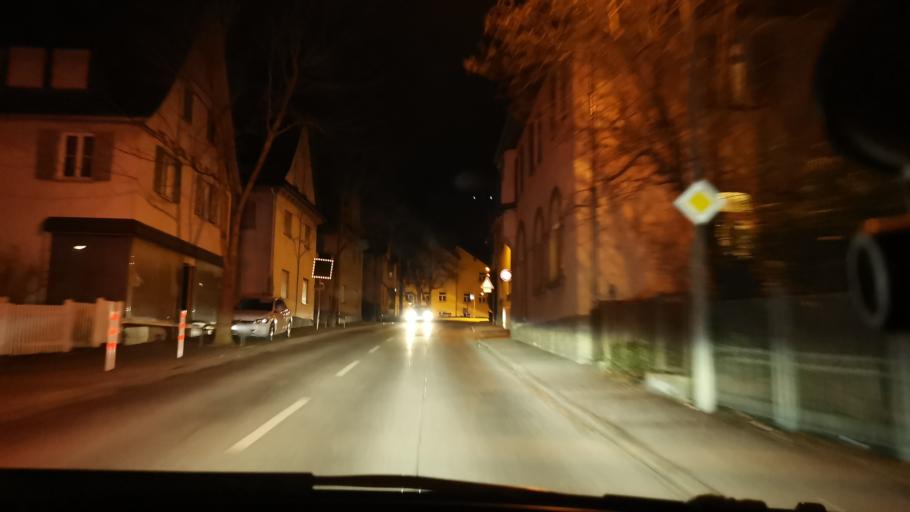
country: DE
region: Baden-Wuerttemberg
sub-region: Regierungsbezirk Stuttgart
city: Ehningen
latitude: 48.6968
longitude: 8.9406
